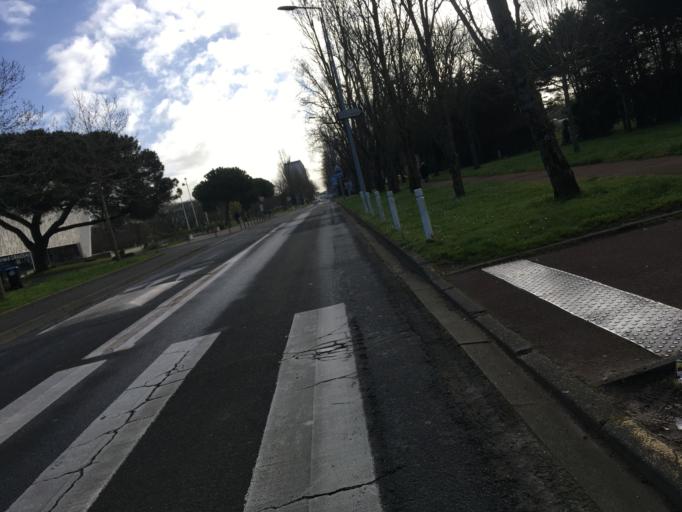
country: FR
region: Poitou-Charentes
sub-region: Departement de la Charente-Maritime
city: La Rochelle
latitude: 46.1681
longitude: -1.1862
